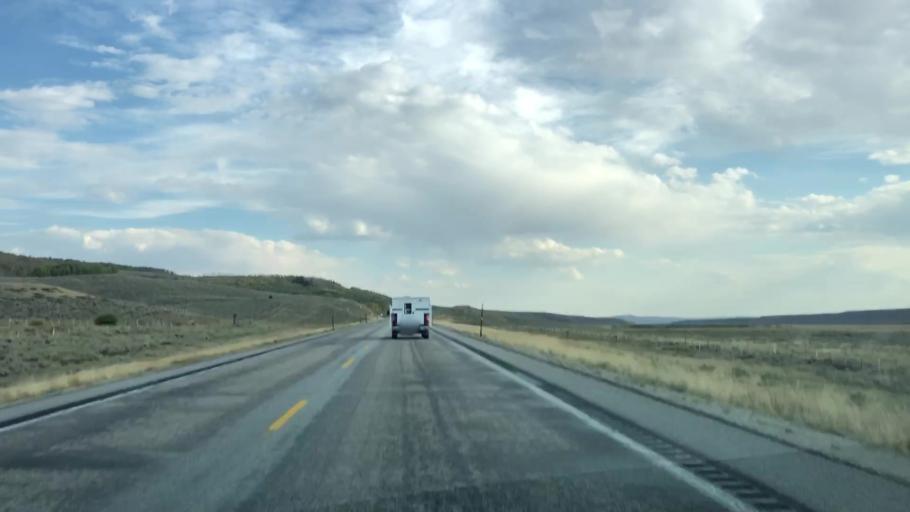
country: US
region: Wyoming
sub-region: Sublette County
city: Pinedale
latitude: 43.0964
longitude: -110.1674
